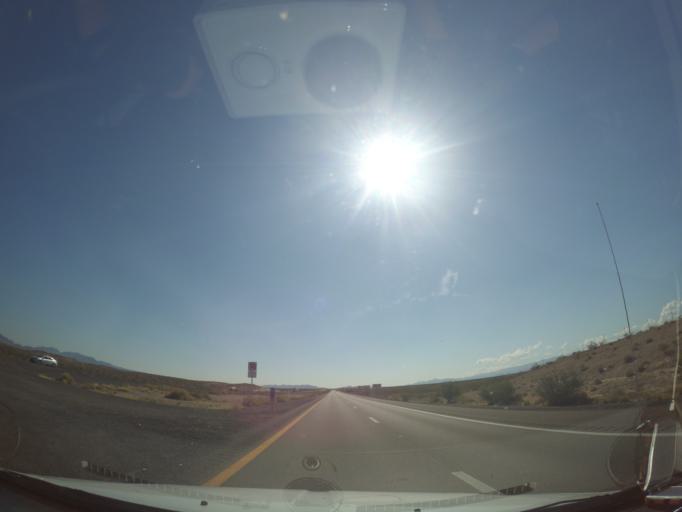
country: US
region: Nevada
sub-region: Clark County
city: Moapa Town
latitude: 36.5306
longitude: -114.7248
